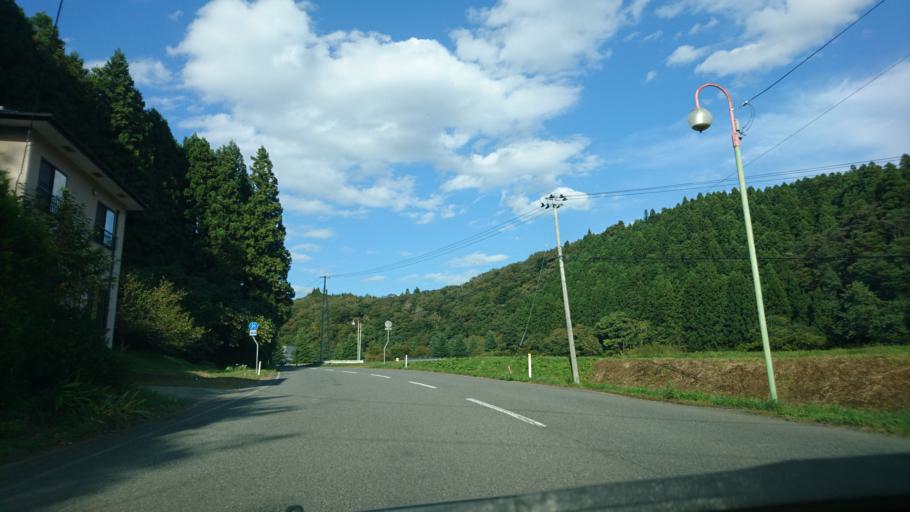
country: JP
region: Iwate
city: Ichinoseki
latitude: 38.8514
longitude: 141.3027
